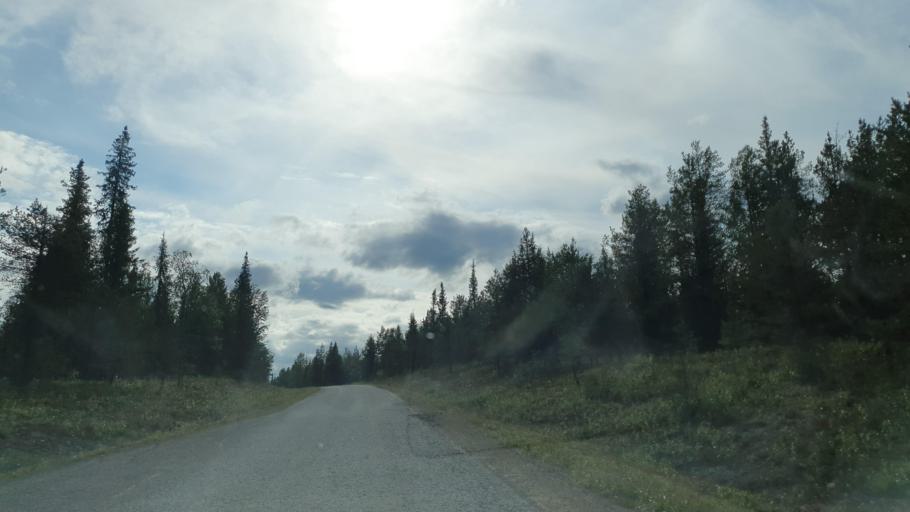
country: FI
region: Lapland
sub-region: Tunturi-Lappi
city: Muonio
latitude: 67.7037
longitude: 24.1215
